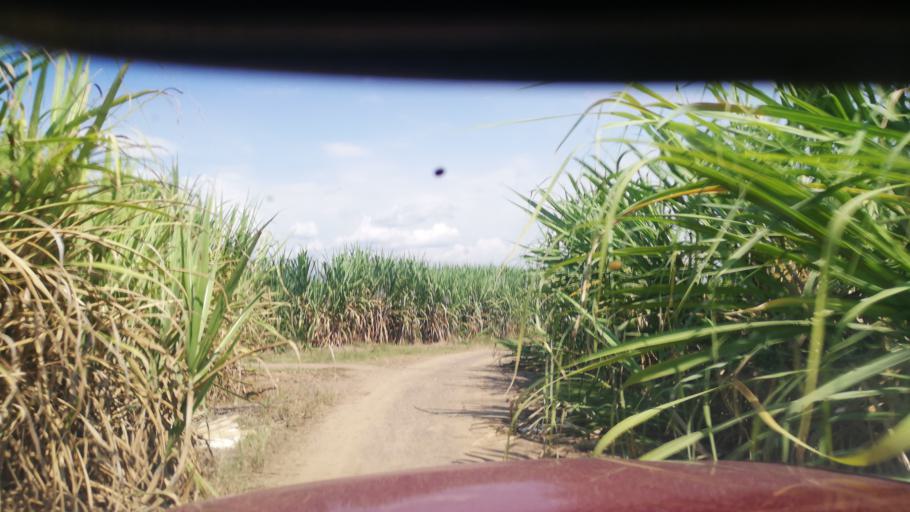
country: CO
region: Risaralda
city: La Virginia
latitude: 4.8998
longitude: -75.9308
